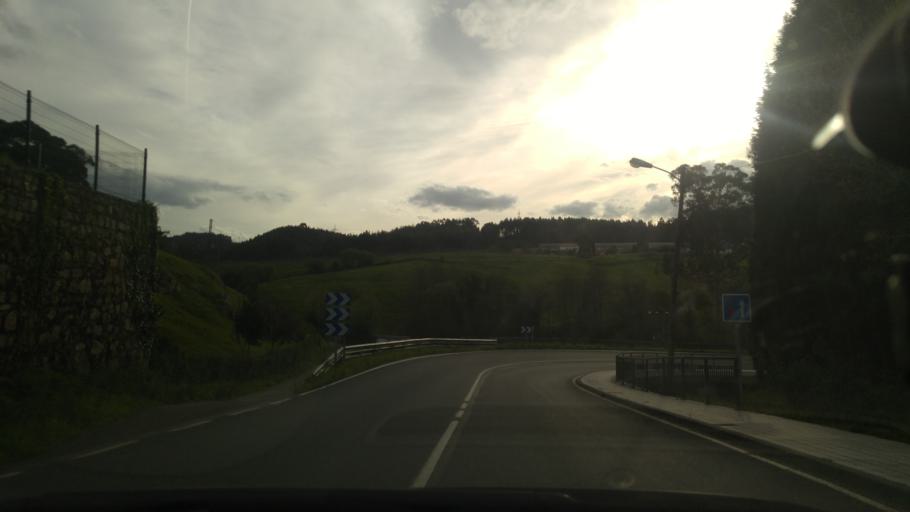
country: ES
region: Asturias
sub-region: Province of Asturias
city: Corvera de Asturias
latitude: 43.5311
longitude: -5.8822
